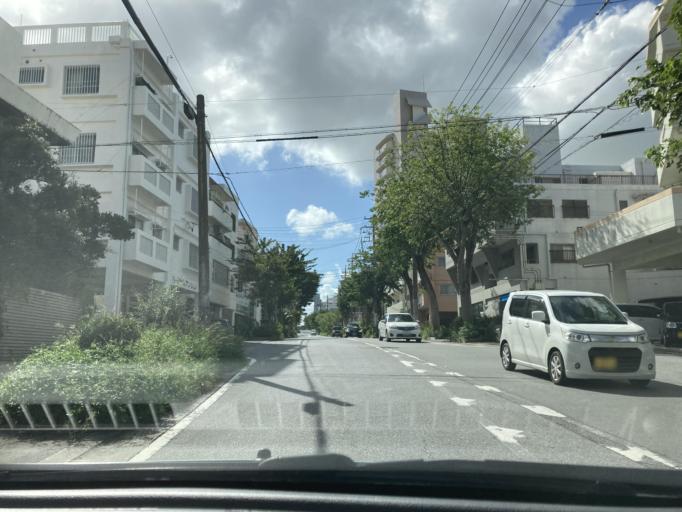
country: JP
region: Okinawa
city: Naha-shi
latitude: 26.2102
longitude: 127.6818
